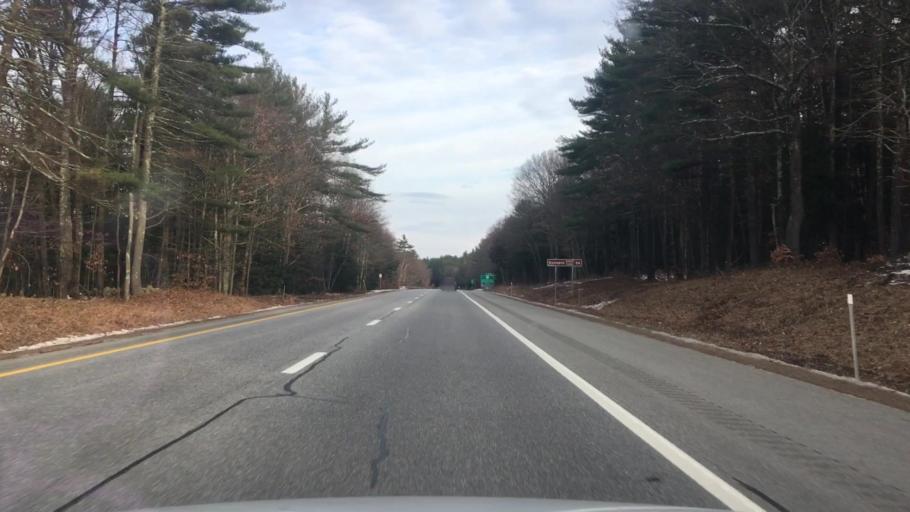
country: US
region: New Hampshire
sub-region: Merrimack County
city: Hopkinton
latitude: 43.1875
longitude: -71.6983
